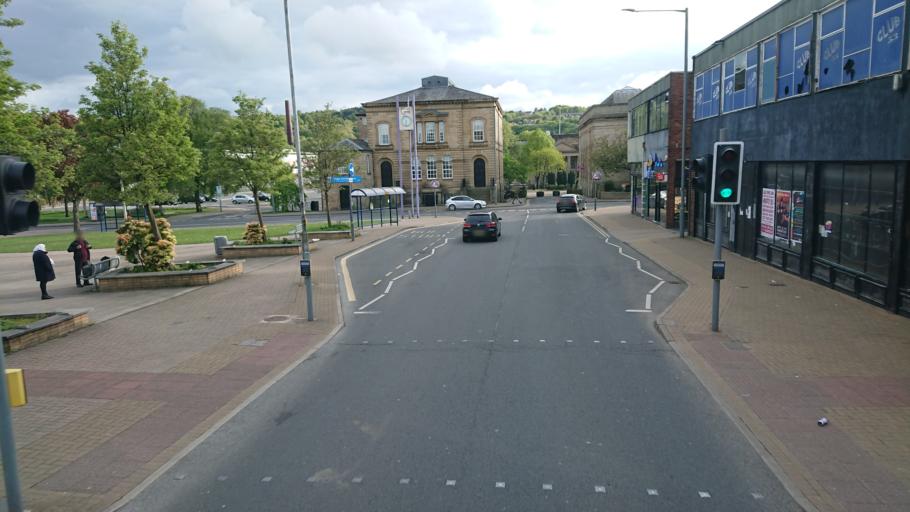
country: GB
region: England
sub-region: Lancashire
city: Burnley
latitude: 53.7883
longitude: -2.2404
